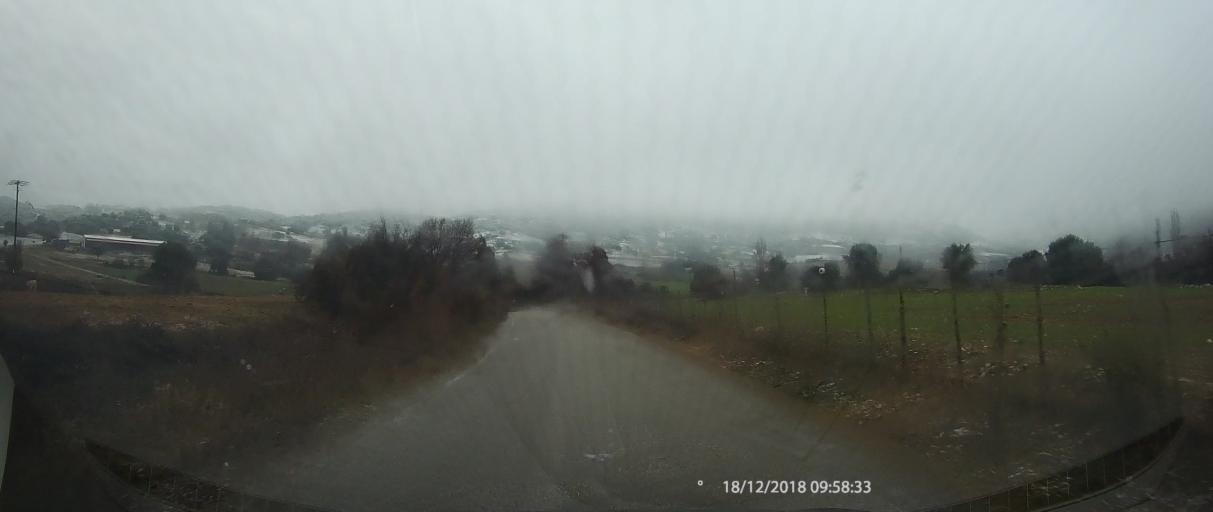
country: GR
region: Thessaly
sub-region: Nomos Larisis
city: Livadi
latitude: 40.0277
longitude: 22.2419
